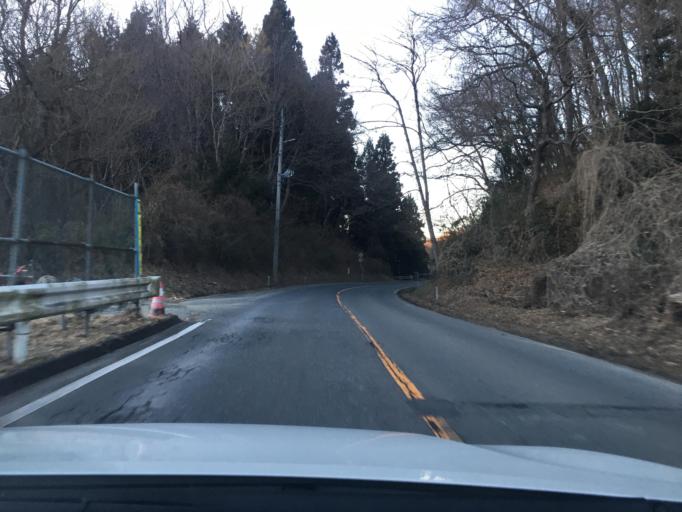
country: JP
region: Fukushima
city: Miharu
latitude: 37.4544
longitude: 140.5064
